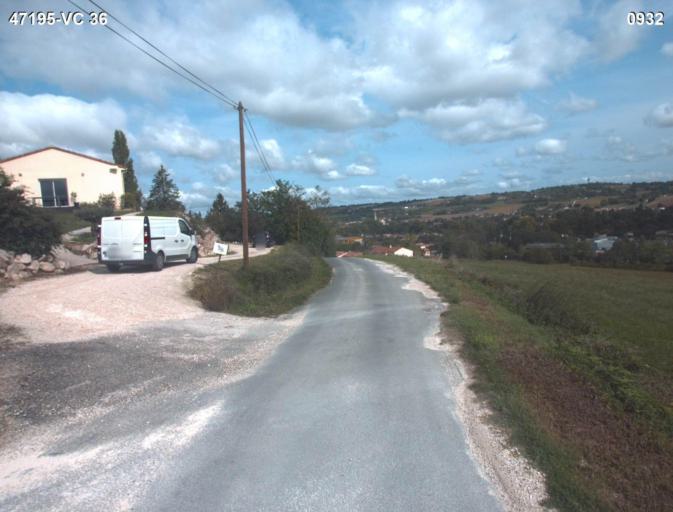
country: FR
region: Aquitaine
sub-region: Departement du Lot-et-Garonne
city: Nerac
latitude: 44.1251
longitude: 0.3356
